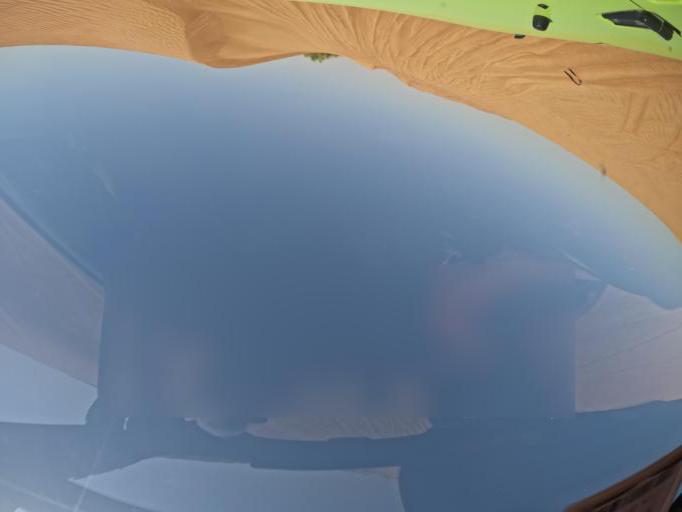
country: AE
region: Ash Shariqah
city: Adh Dhayd
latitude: 24.9659
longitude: 55.7206
